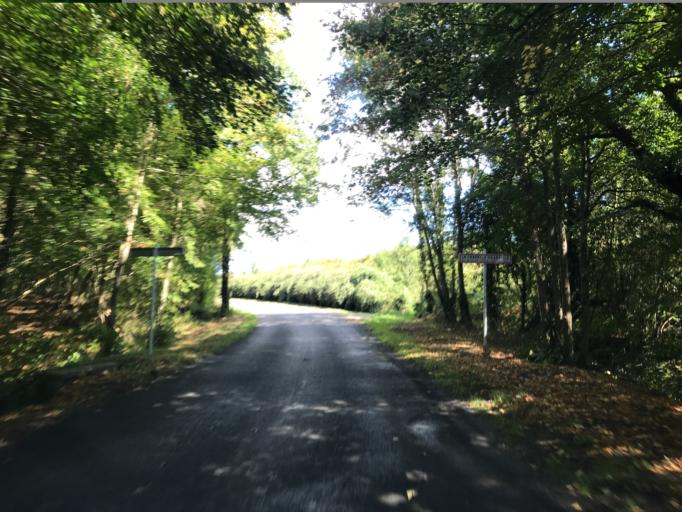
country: FR
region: Haute-Normandie
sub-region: Departement de l'Eure
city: La Chapelle-Reanville
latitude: 49.0874
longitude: 1.3960
